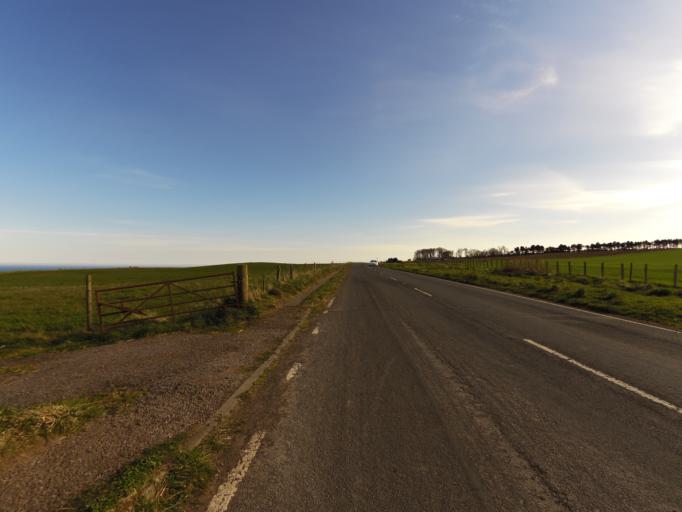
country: GB
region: Scotland
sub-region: Aberdeenshire
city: Stonehaven
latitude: 56.9496
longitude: -2.2051
